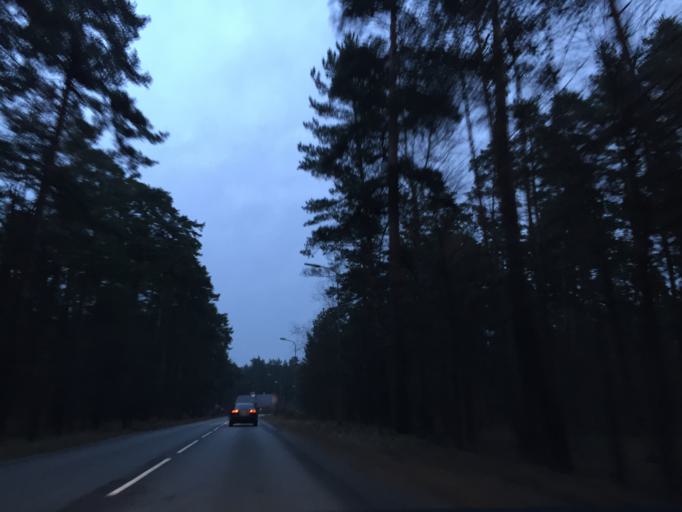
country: LV
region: Riga
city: Jaunciems
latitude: 57.0438
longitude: 24.1158
